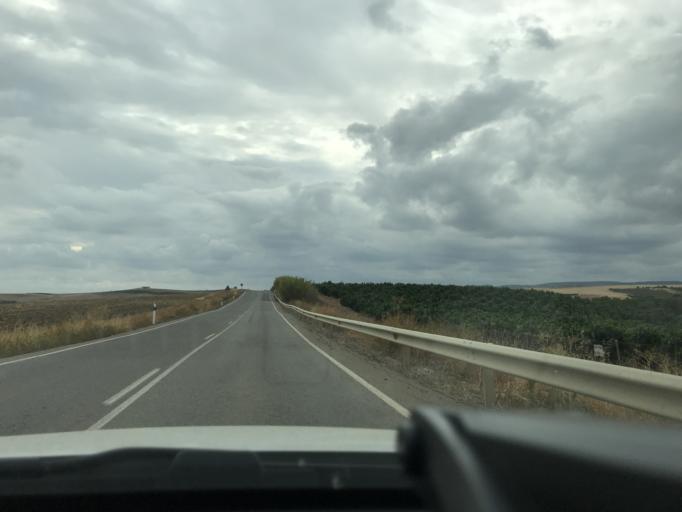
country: ES
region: Andalusia
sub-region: Provincia de Sevilla
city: Cantillana
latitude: 37.6271
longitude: -5.7800
